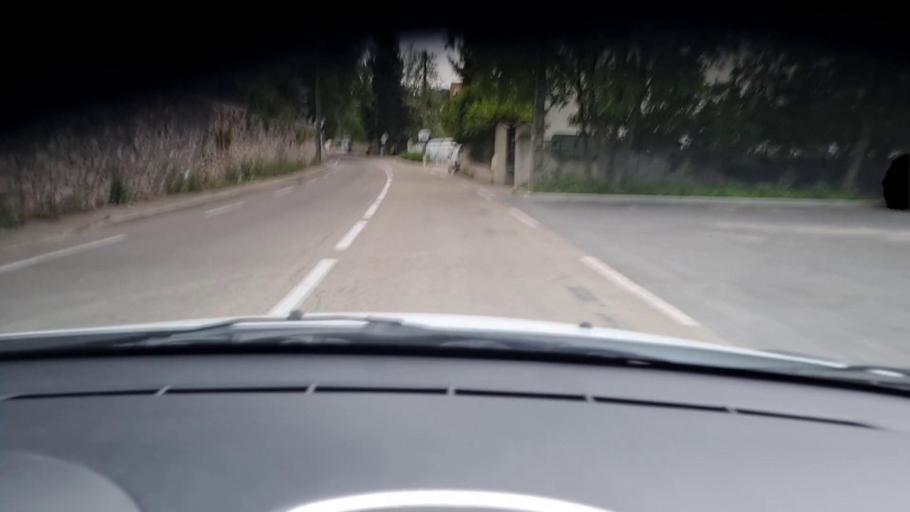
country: FR
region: Languedoc-Roussillon
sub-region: Departement du Gard
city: Nimes
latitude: 43.8568
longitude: 4.3785
